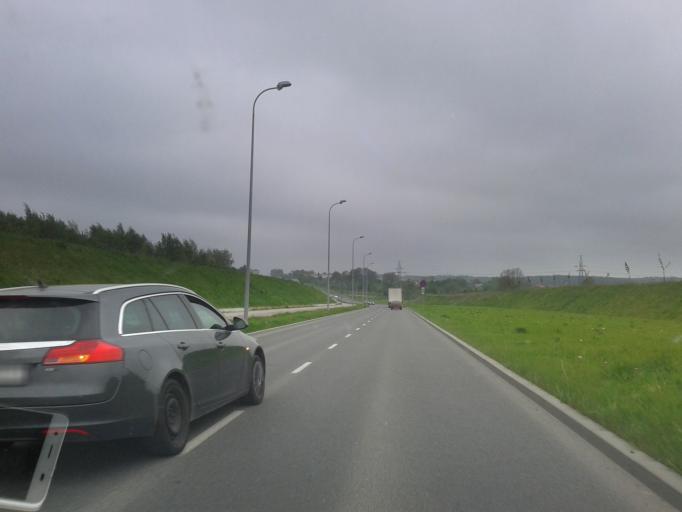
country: PL
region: West Pomeranian Voivodeship
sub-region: Koszalin
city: Koszalin
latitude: 54.2130
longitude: 16.1758
